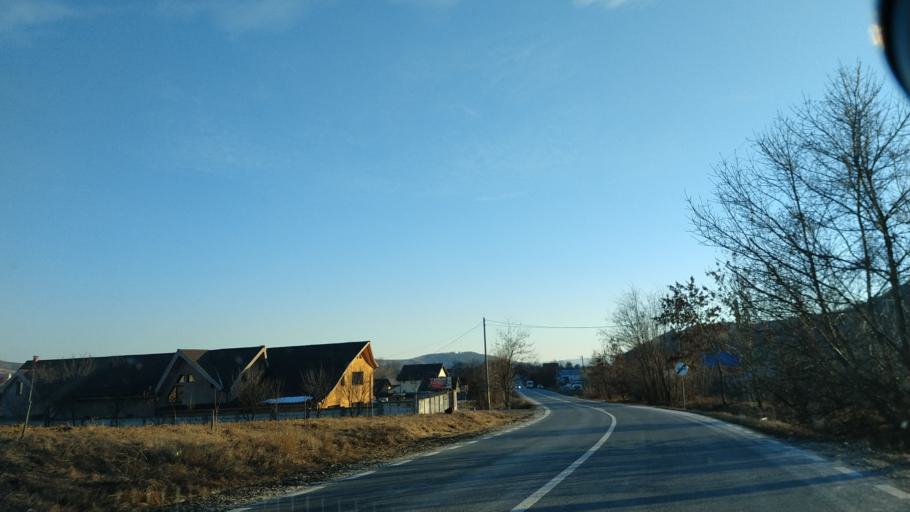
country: RO
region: Bacau
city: Gura Vaii
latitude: 46.3237
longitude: 26.7452
